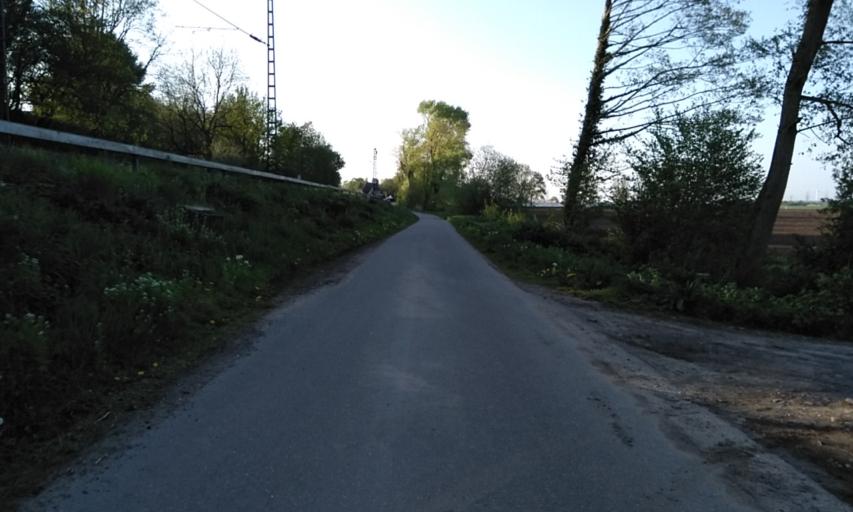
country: DE
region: Lower Saxony
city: Dollern
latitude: 53.5424
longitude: 9.5604
